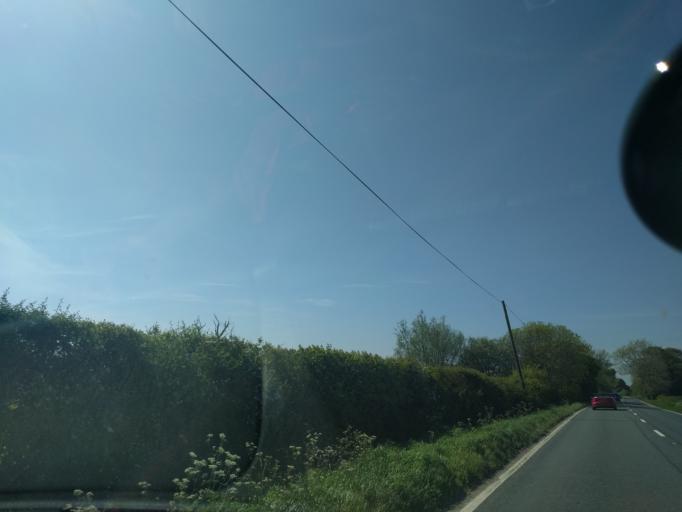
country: GB
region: England
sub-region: Somerset
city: Ilchester
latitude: 51.0327
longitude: -2.6601
